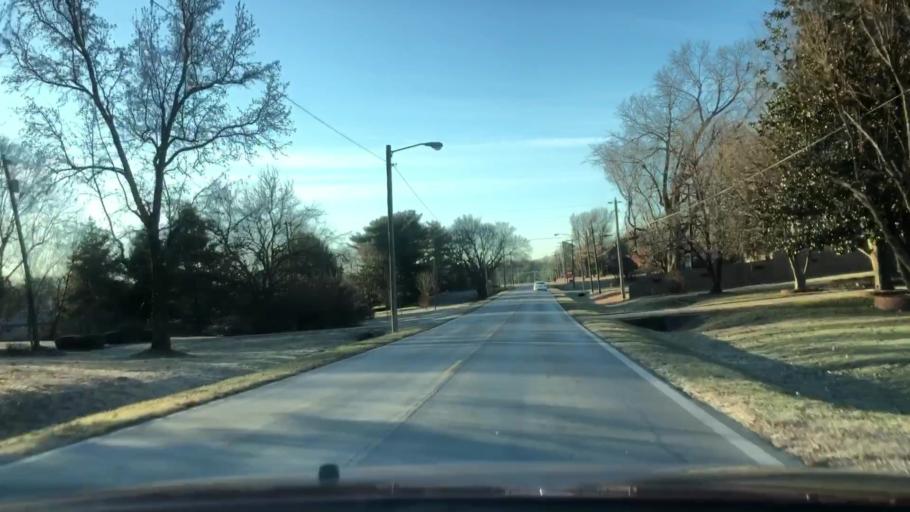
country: US
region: Missouri
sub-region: Greene County
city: Springfield
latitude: 37.1720
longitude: -93.2466
